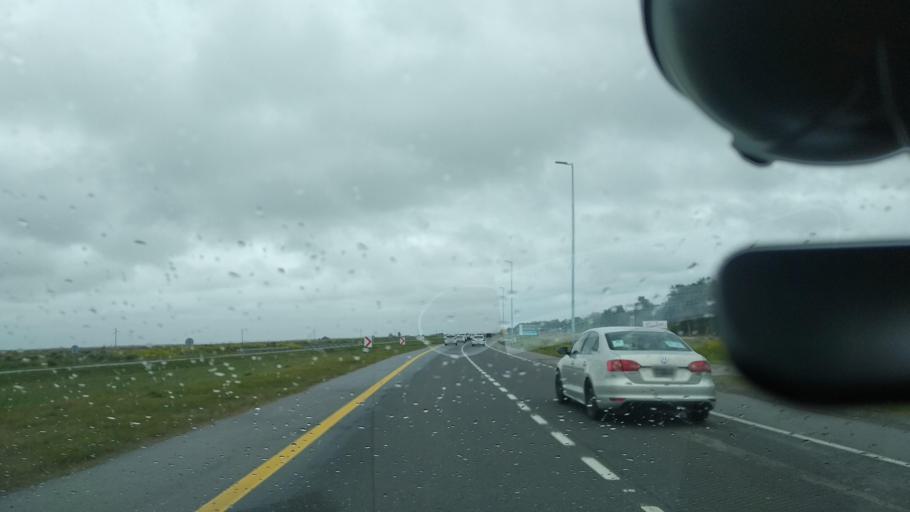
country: AR
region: Buenos Aires
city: San Clemente del Tuyu
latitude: -36.3896
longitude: -56.7447
